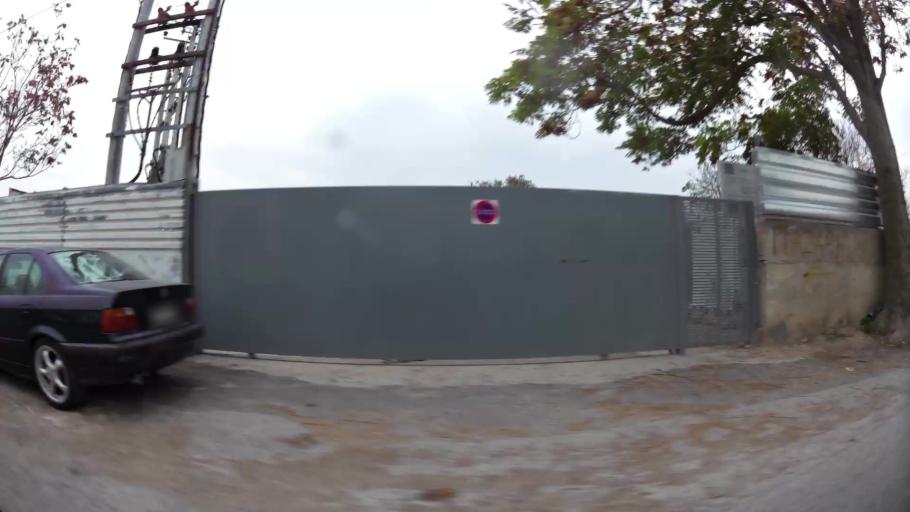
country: GR
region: Attica
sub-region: Nomarchia Athinas
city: Aigaleo
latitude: 37.9834
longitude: 23.6978
